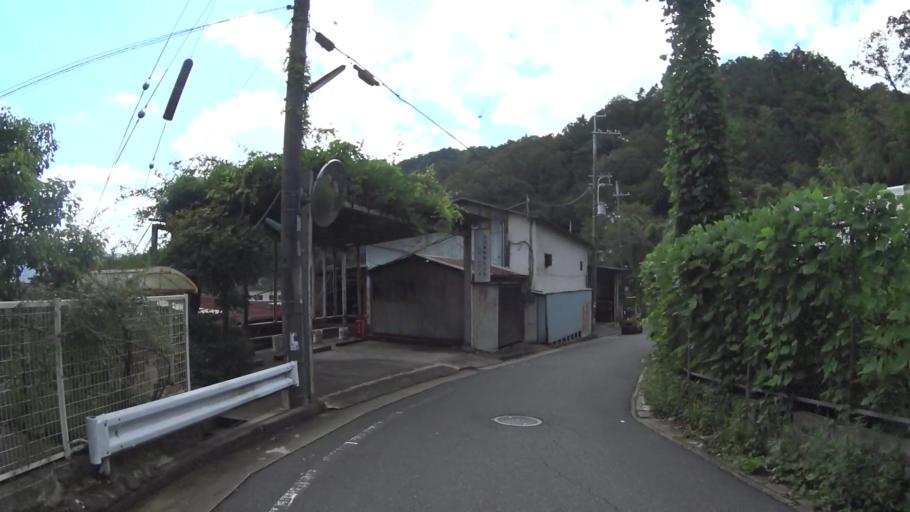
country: JP
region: Kyoto
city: Kyoto
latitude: 34.9748
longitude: 135.7913
